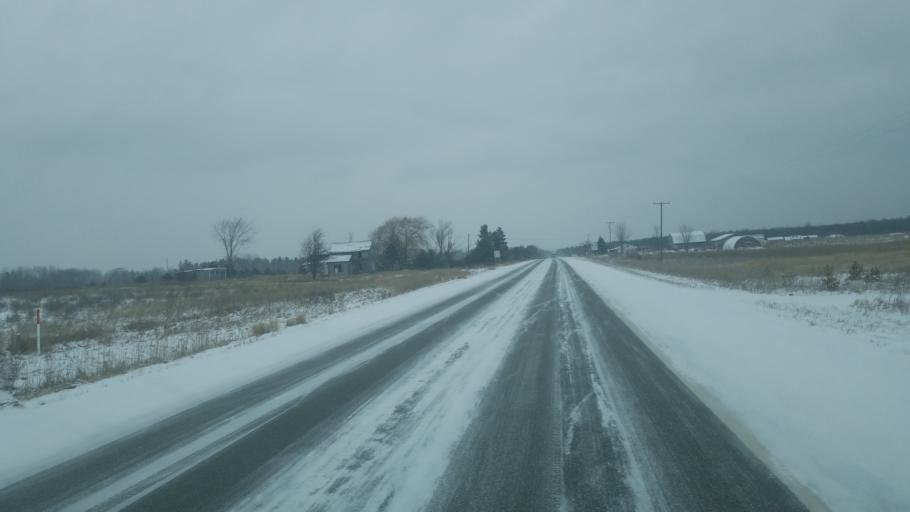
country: US
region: Michigan
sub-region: Osceola County
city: Evart
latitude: 43.9277
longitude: -85.1484
